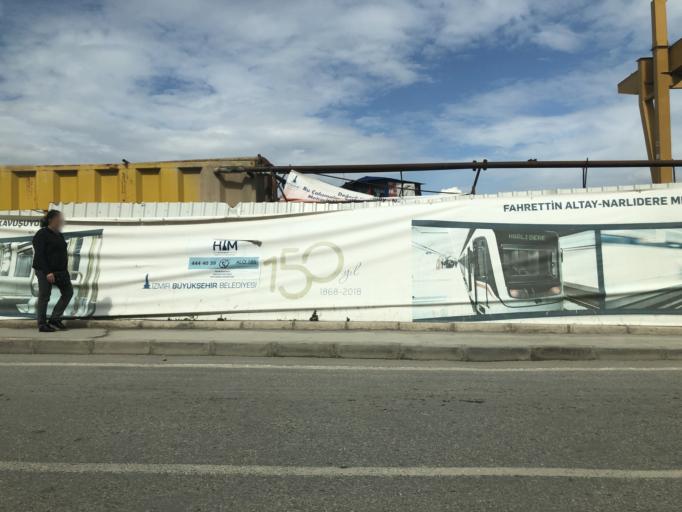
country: TR
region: Izmir
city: Karsiyaka
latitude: 38.3941
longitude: 27.0458
